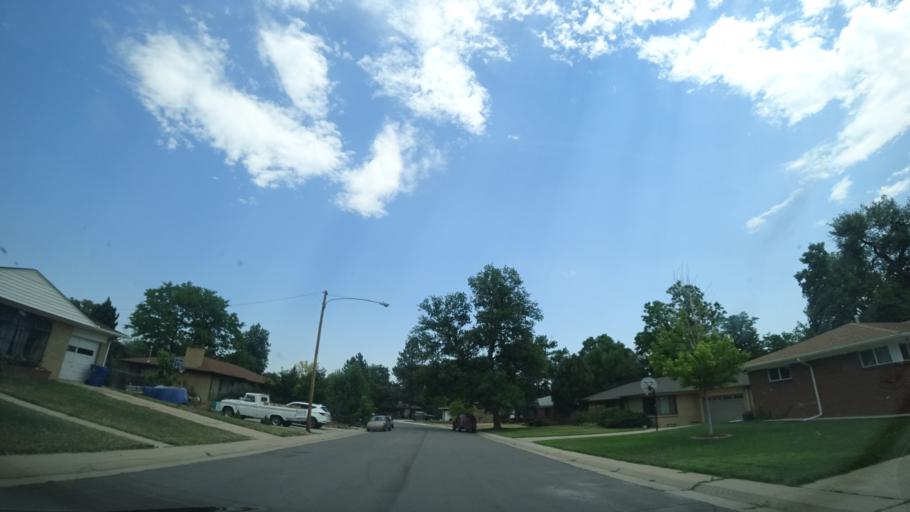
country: US
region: Colorado
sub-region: Jefferson County
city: Lakewood
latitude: 39.7208
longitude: -105.0994
